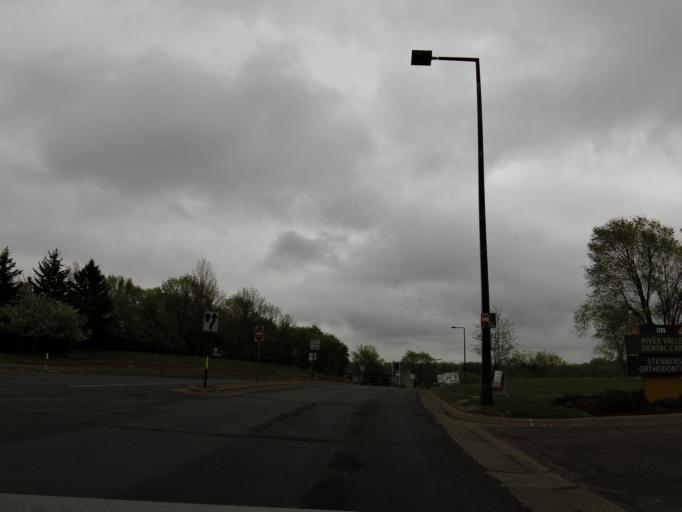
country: US
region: Minnesota
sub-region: Washington County
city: Stillwater
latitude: 45.0414
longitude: -92.8266
